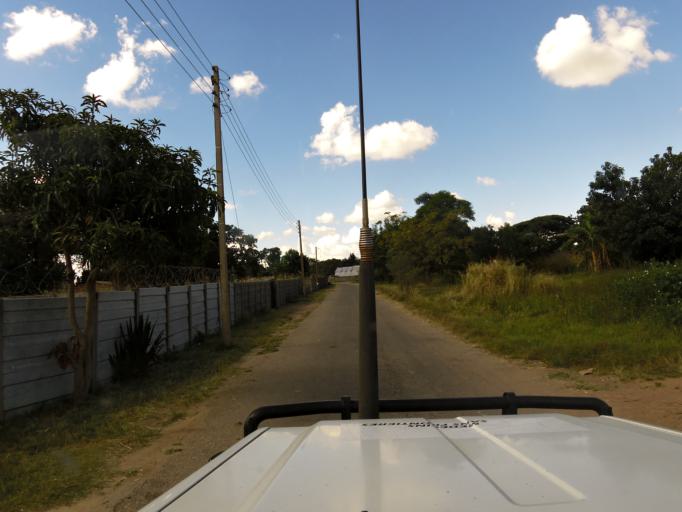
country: ZW
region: Harare
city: Epworth
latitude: -17.8709
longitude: 31.1302
